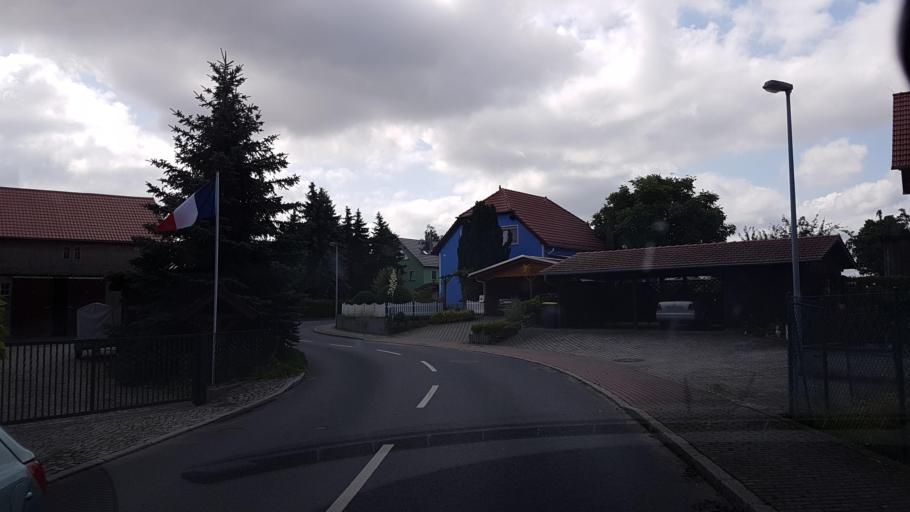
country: DE
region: Saxony
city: Wachau
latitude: 51.1875
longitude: 13.9054
